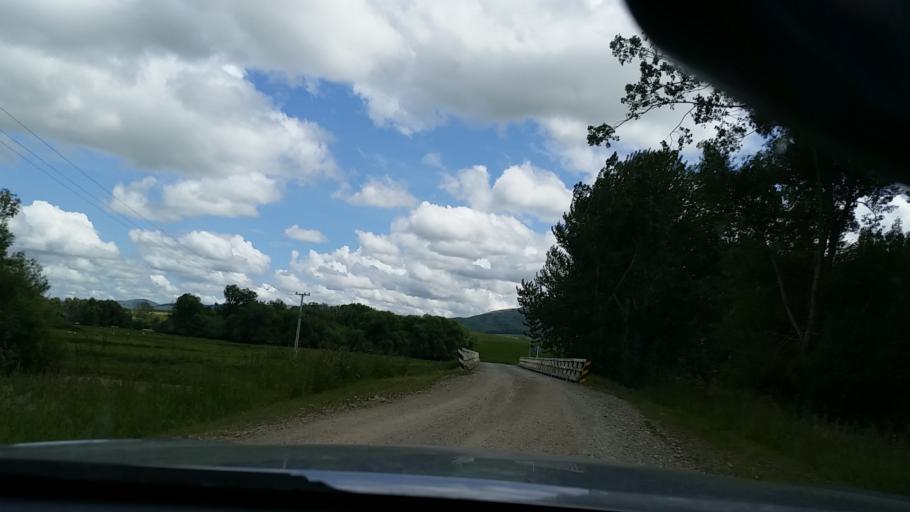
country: NZ
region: Otago
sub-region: Queenstown-Lakes District
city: Kingston
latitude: -45.6675
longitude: 168.8981
